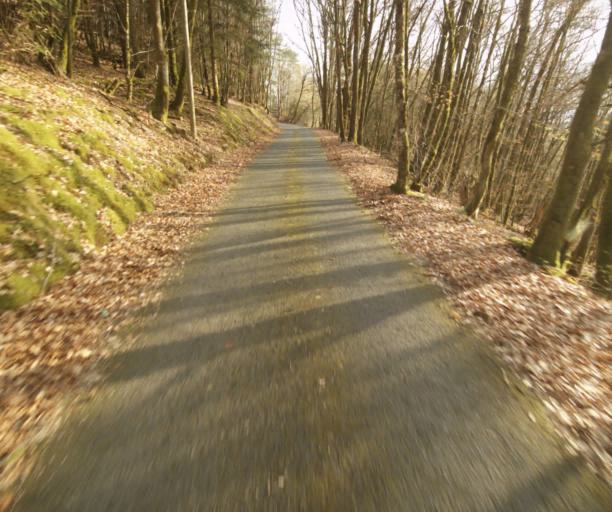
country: FR
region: Limousin
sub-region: Departement de la Correze
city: Correze
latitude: 45.3524
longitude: 1.8240
